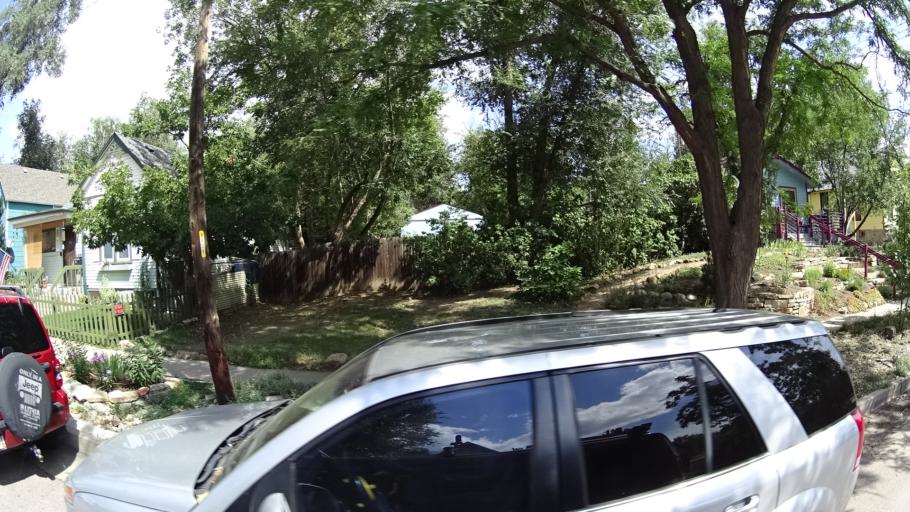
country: US
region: Colorado
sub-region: El Paso County
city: Colorado Springs
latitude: 38.8365
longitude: -104.8104
